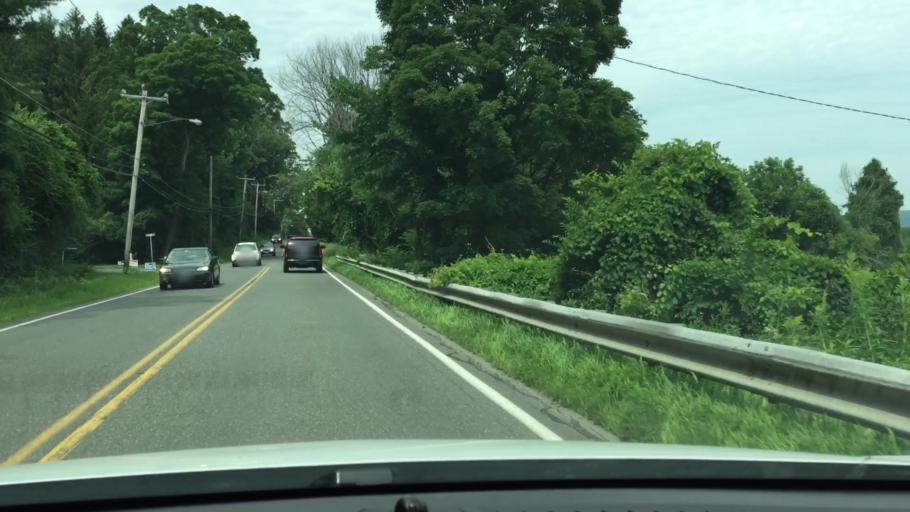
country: US
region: Massachusetts
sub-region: Berkshire County
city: Pittsfield
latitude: 42.4132
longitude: -73.2495
